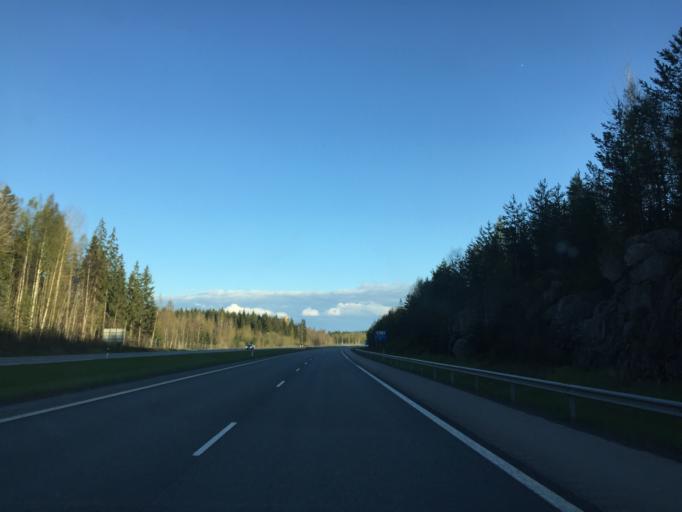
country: FI
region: Haeme
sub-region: Riihimaeki
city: Riihimaeki
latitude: 60.7606
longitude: 24.7252
